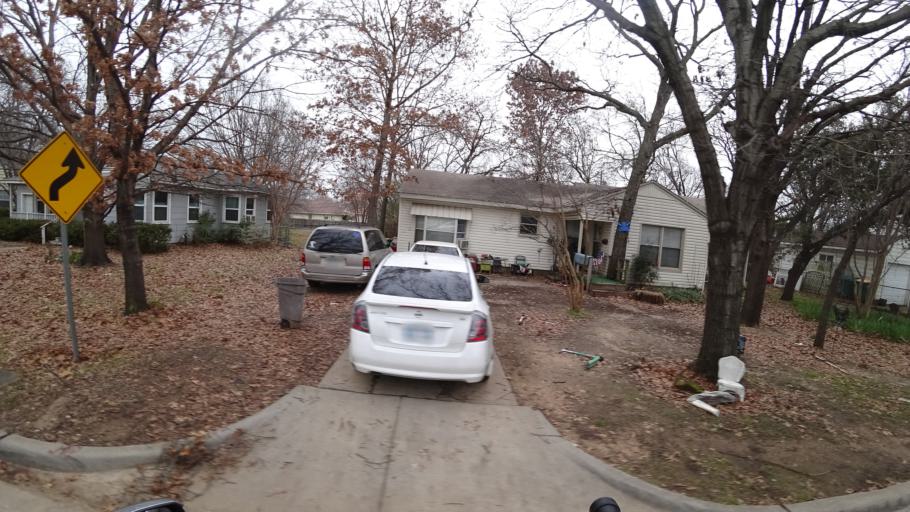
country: US
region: Texas
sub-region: Denton County
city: Lewisville
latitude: 33.0507
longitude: -97.0037
